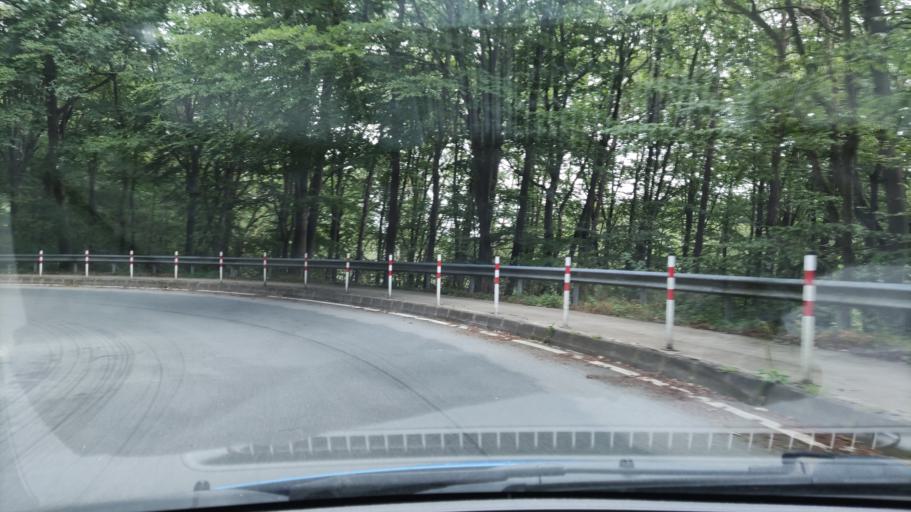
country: DE
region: Lower Saxony
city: Schnega
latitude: 52.9296
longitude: 10.9126
